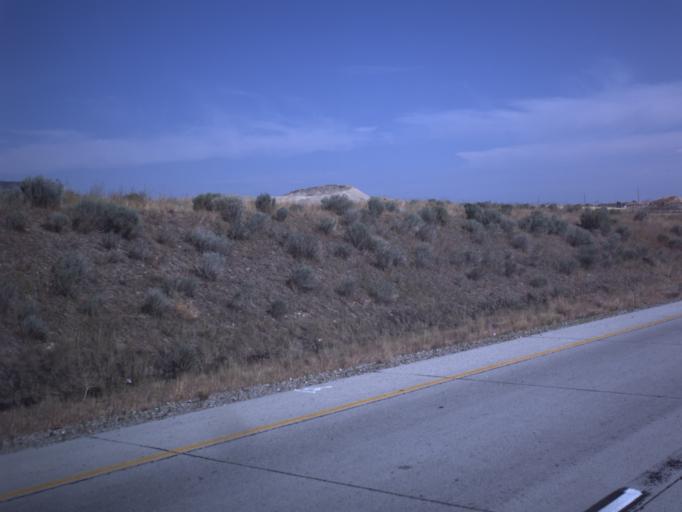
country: US
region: Utah
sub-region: Salt Lake County
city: Oquirrh
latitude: 40.6407
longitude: -112.0446
